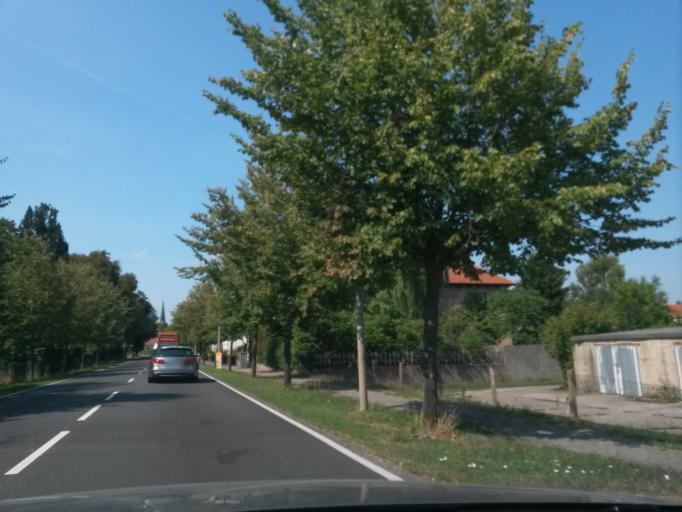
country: DE
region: Saxony-Anhalt
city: Jerichow
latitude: 52.4943
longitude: 12.0293
